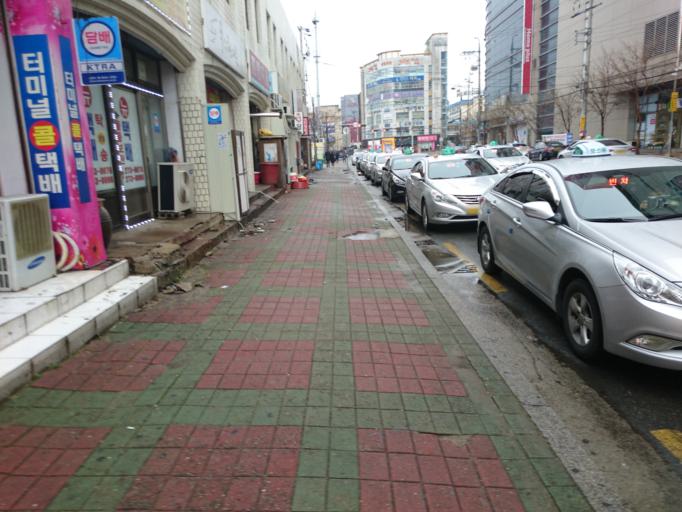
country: KR
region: Gyeongsangbuk-do
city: Enjitsu
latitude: 36.0133
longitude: 129.3490
